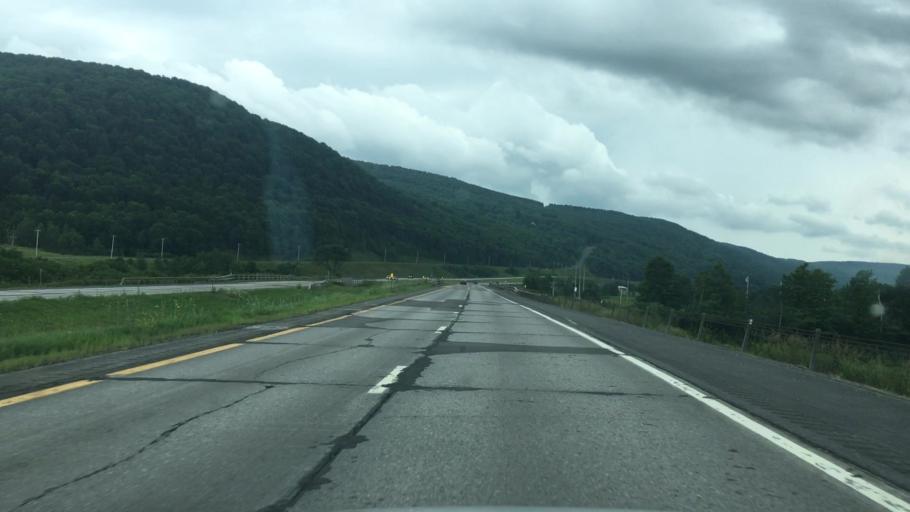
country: US
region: New York
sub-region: Otsego County
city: Worcester
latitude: 42.6301
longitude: -74.6600
